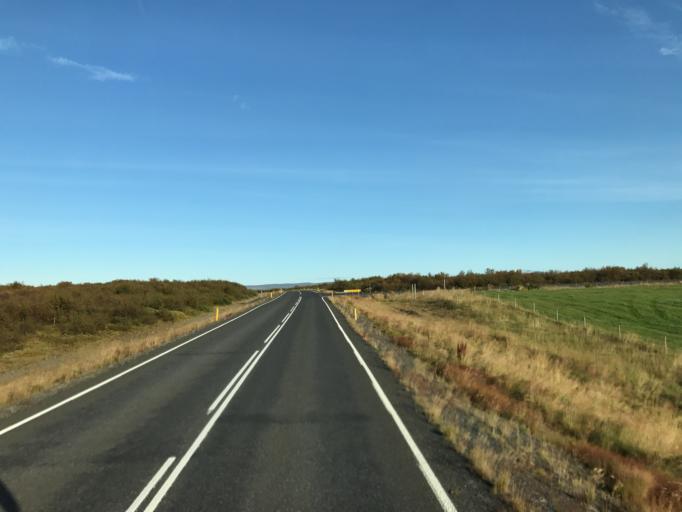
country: IS
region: South
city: Selfoss
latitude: 64.2250
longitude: -20.5889
